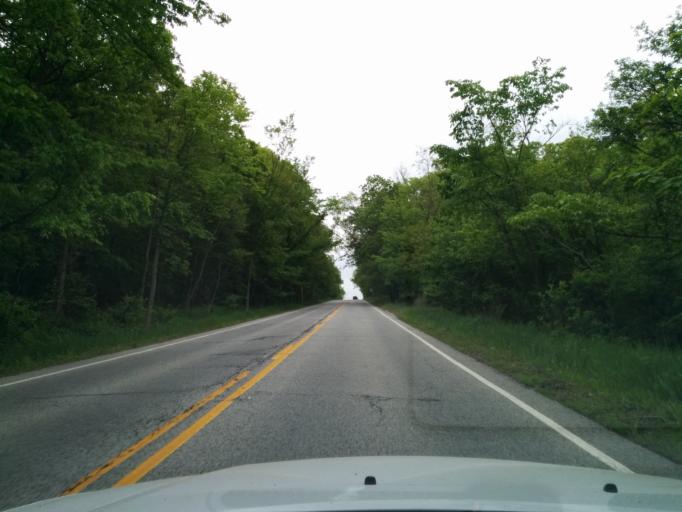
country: US
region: Illinois
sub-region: Cook County
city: Willow Springs
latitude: 41.7234
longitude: -87.8761
